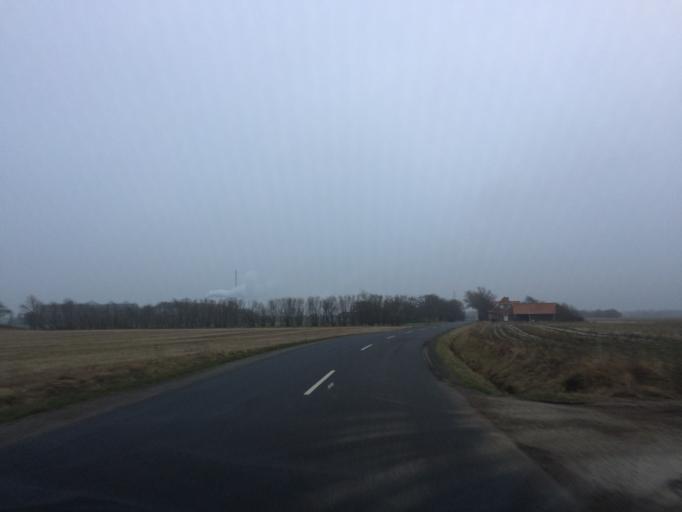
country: DK
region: South Denmark
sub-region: Varde Kommune
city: Oksbol
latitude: 55.7829
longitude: 8.3128
